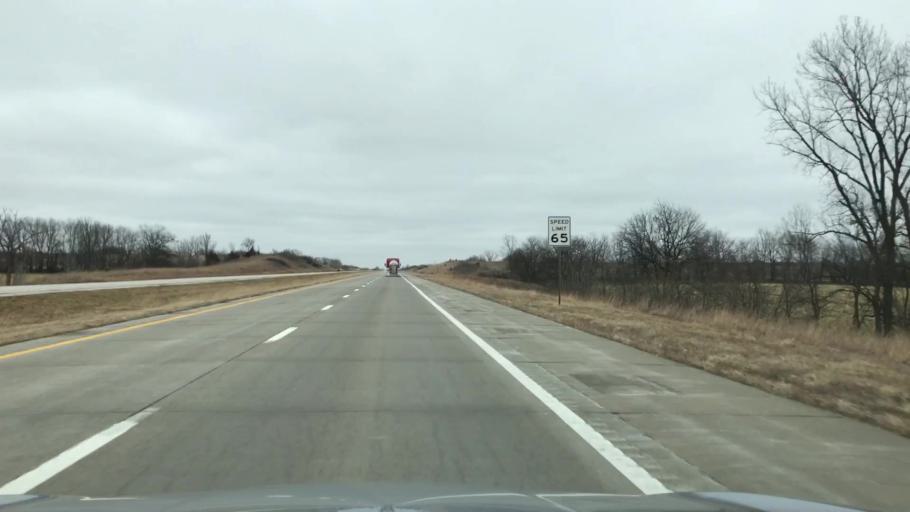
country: US
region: Missouri
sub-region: Caldwell County
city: Hamilton
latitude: 39.7344
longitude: -93.9620
